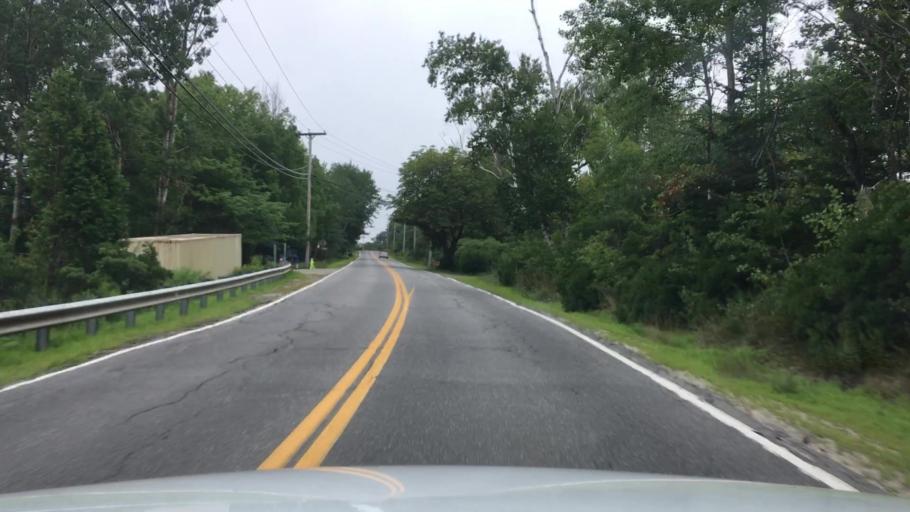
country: US
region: Maine
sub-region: Cumberland County
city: Harpswell Center
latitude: 43.7729
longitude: -69.9682
